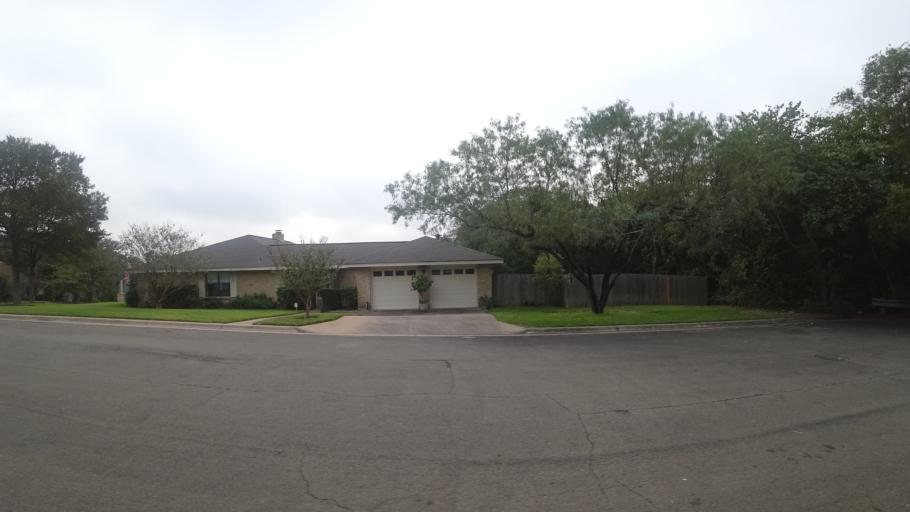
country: US
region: Texas
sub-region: Travis County
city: Wells Branch
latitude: 30.3657
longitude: -97.6660
